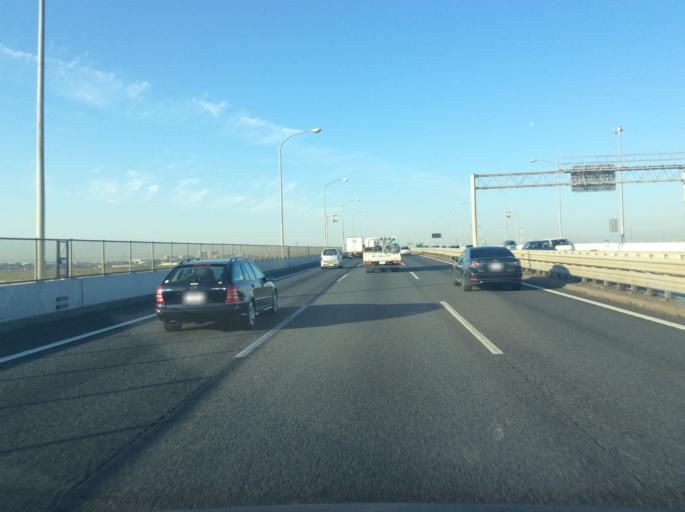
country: JP
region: Chiba
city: Nagareyama
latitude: 35.8768
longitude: 139.8975
